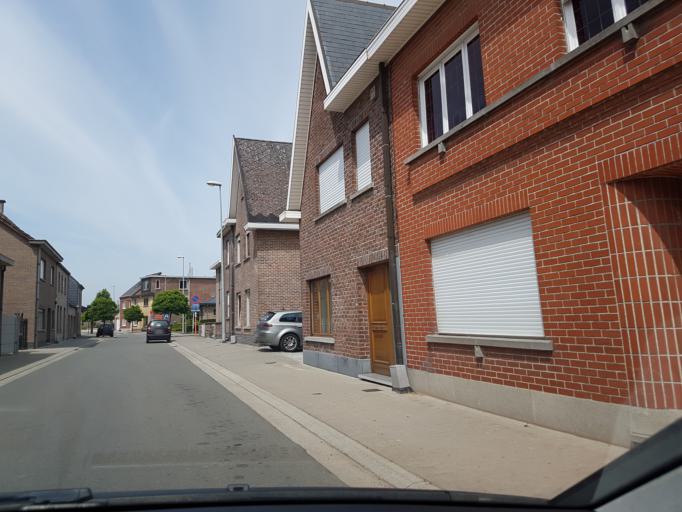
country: BE
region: Flanders
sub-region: Provincie Oost-Vlaanderen
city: Denderleeuw
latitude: 50.9203
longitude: 4.1071
